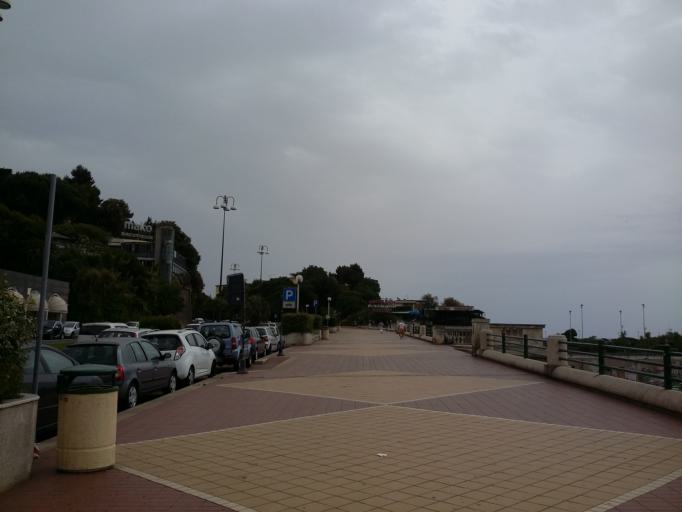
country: IT
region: Liguria
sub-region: Provincia di Genova
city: San Teodoro
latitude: 44.3937
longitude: 8.9504
